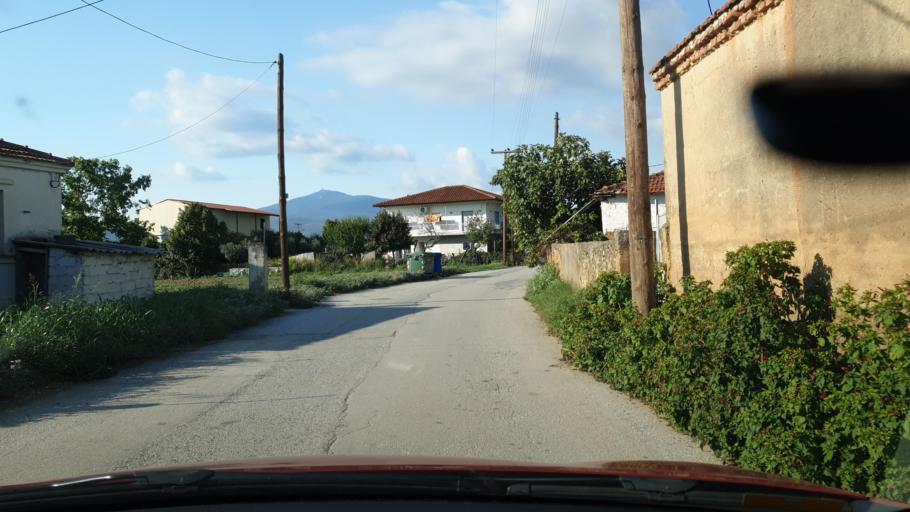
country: GR
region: Central Macedonia
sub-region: Nomos Thessalonikis
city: Vasilika
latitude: 40.4876
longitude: 23.1381
